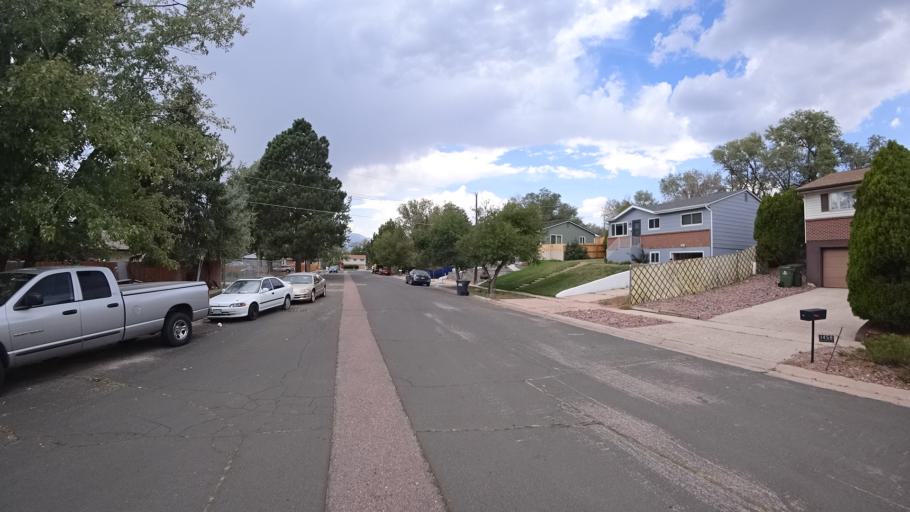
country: US
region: Colorado
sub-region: El Paso County
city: Cimarron Hills
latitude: 38.8538
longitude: -104.7596
